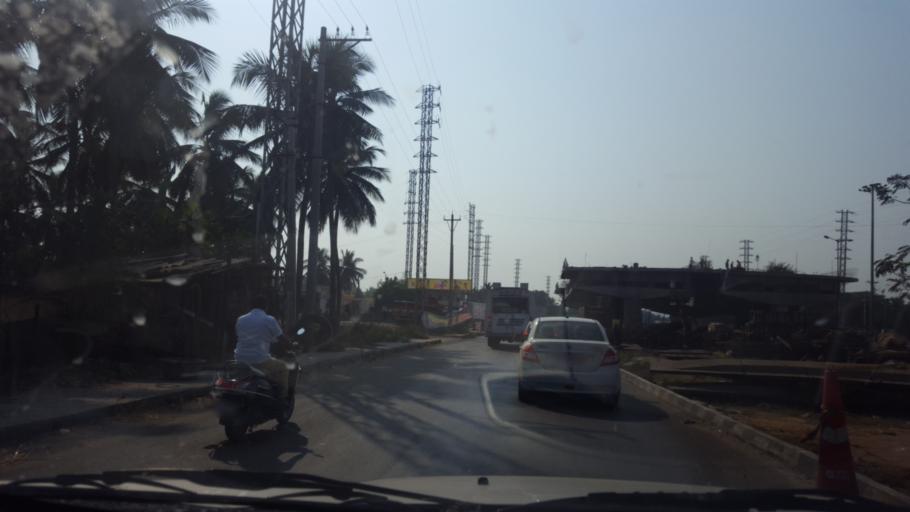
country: IN
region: Andhra Pradesh
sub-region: Vishakhapatnam
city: Anakapalle
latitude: 17.6745
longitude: 83.0018
